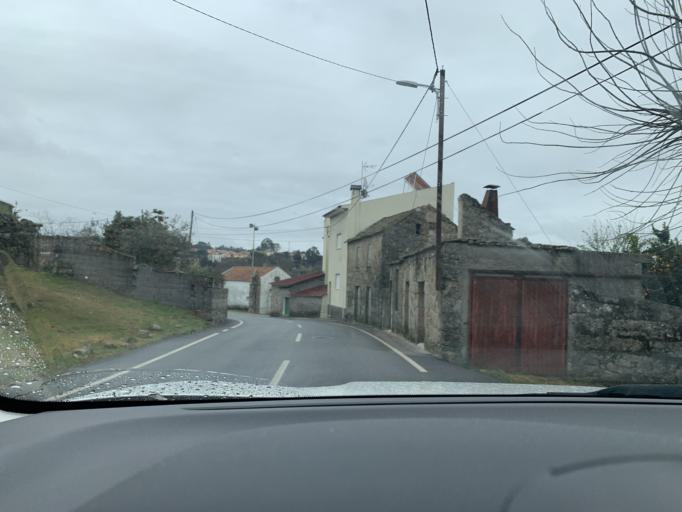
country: PT
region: Viseu
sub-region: Mangualde
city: Mangualde
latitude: 40.6012
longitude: -7.7841
